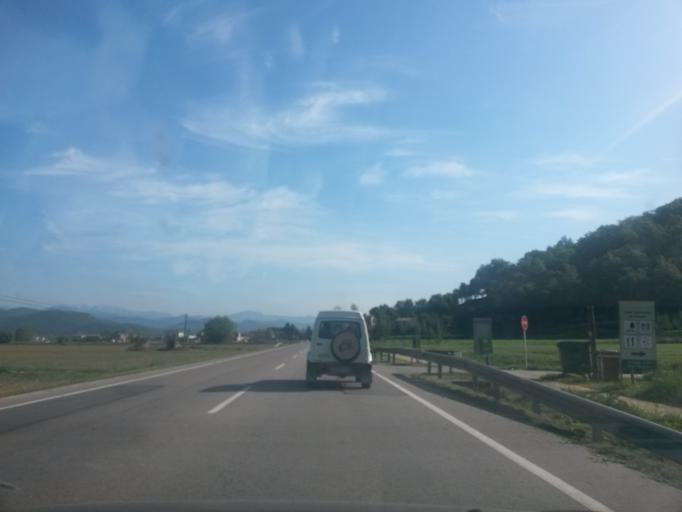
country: ES
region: Catalonia
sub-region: Provincia de Girona
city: Bas
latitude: 42.1360
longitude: 2.4540
